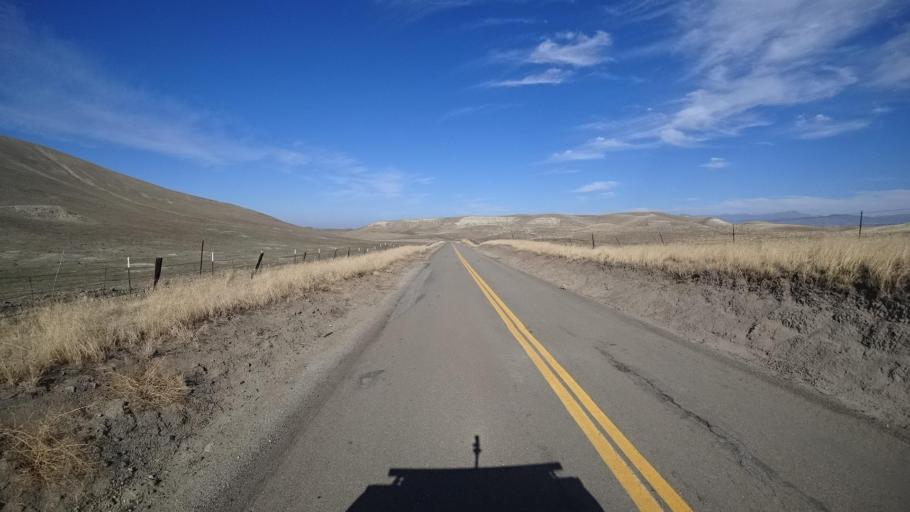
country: US
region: California
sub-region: Kern County
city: Oildale
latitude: 35.6209
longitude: -118.9412
